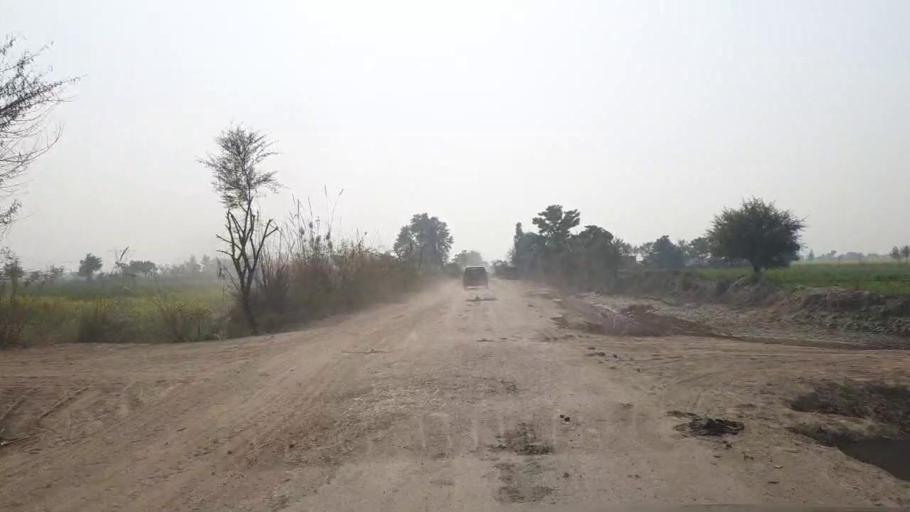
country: PK
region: Sindh
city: Hala
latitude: 25.9326
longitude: 68.4478
